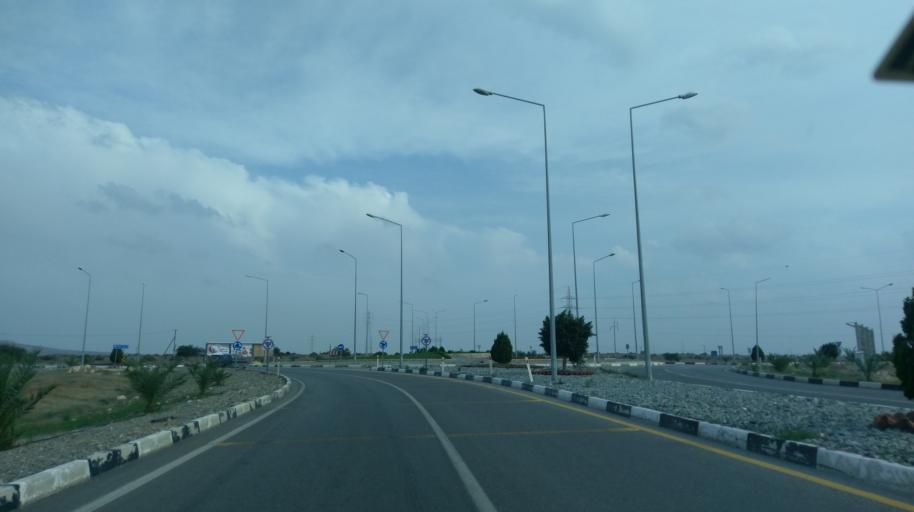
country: CY
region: Lefkosia
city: Astromeritis
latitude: 35.1961
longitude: 33.0634
